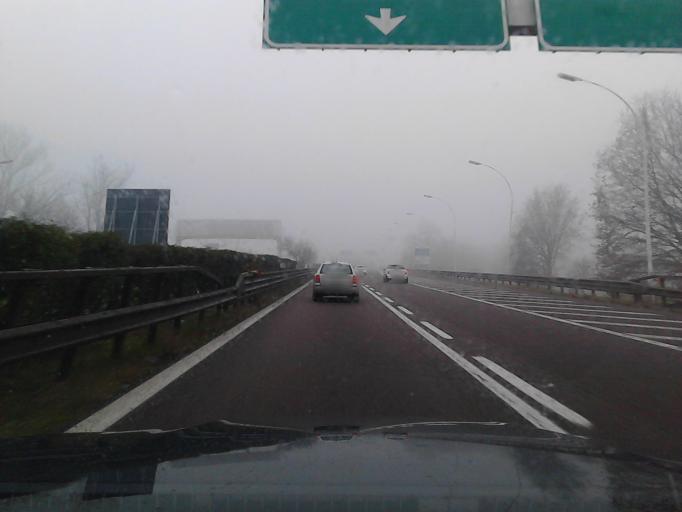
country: IT
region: Emilia-Romagna
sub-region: Provincia di Modena
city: Campogalliano
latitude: 44.6734
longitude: 10.8458
